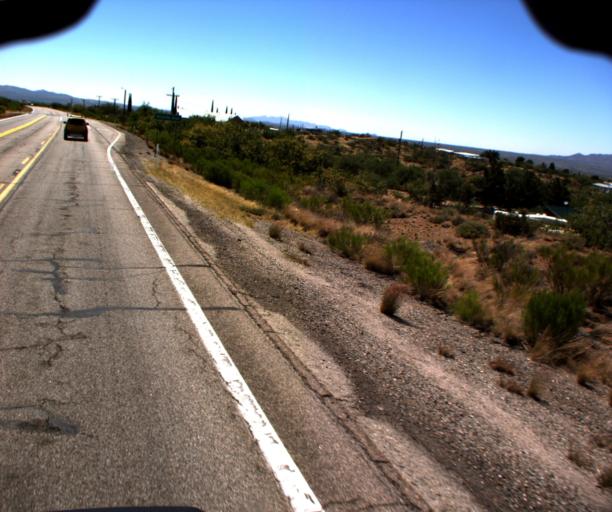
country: US
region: Arizona
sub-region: Pinal County
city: Oracle
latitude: 32.6224
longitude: -110.7939
